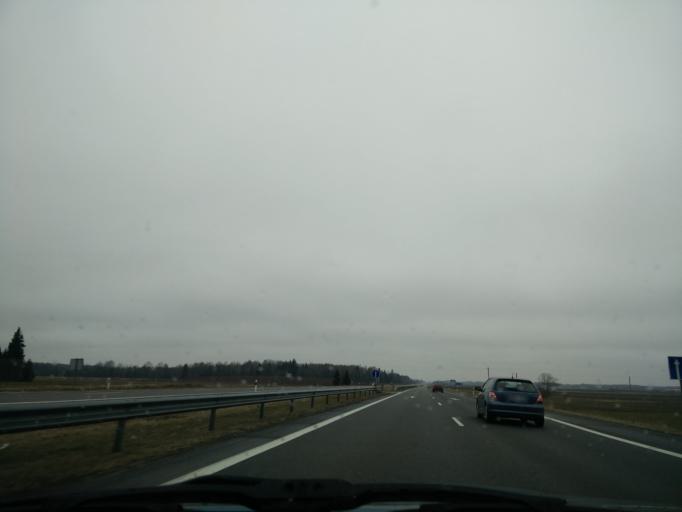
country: LT
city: Raseiniai
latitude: 55.3728
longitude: 22.9549
